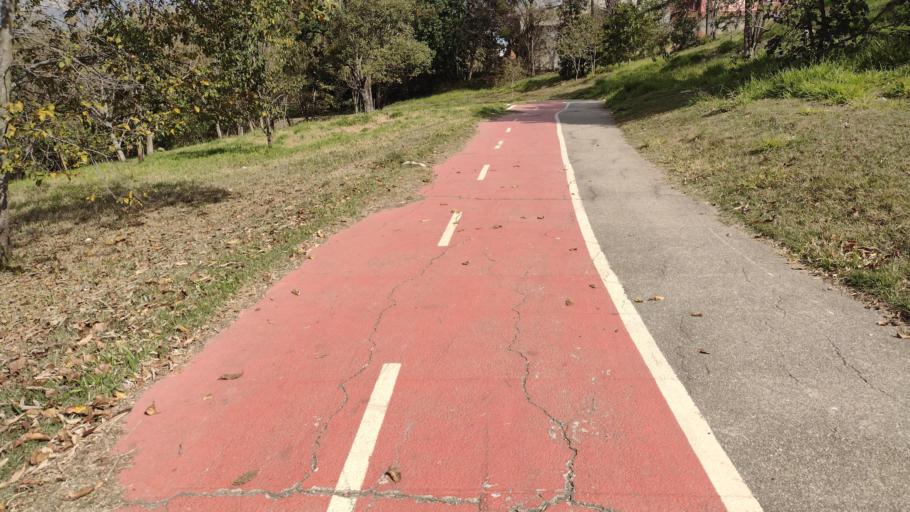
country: BR
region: Sao Paulo
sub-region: Sorocaba
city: Sorocaba
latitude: -23.4507
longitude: -47.4650
